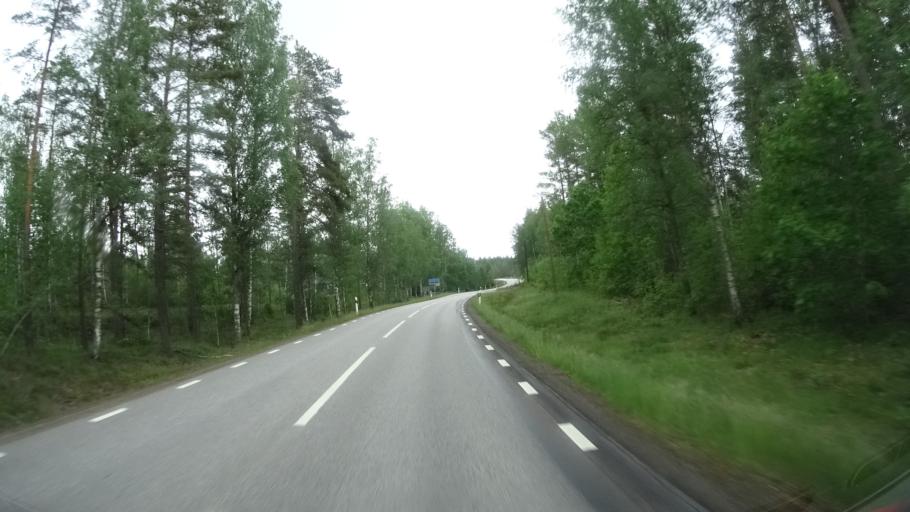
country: SE
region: Kalmar
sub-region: Hultsfreds Kommun
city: Hultsfred
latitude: 57.5338
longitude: 15.7691
